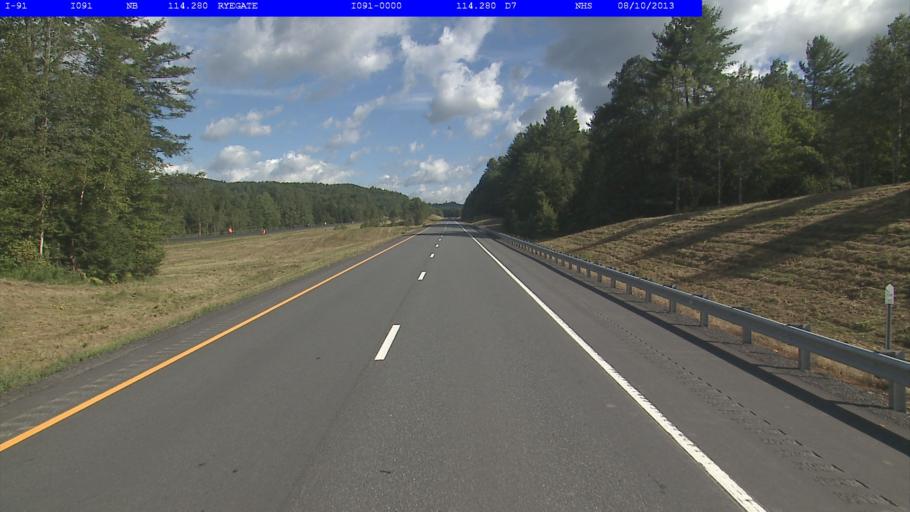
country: US
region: New Hampshire
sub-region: Grafton County
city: Woodsville
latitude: 44.2143
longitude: -72.0670
